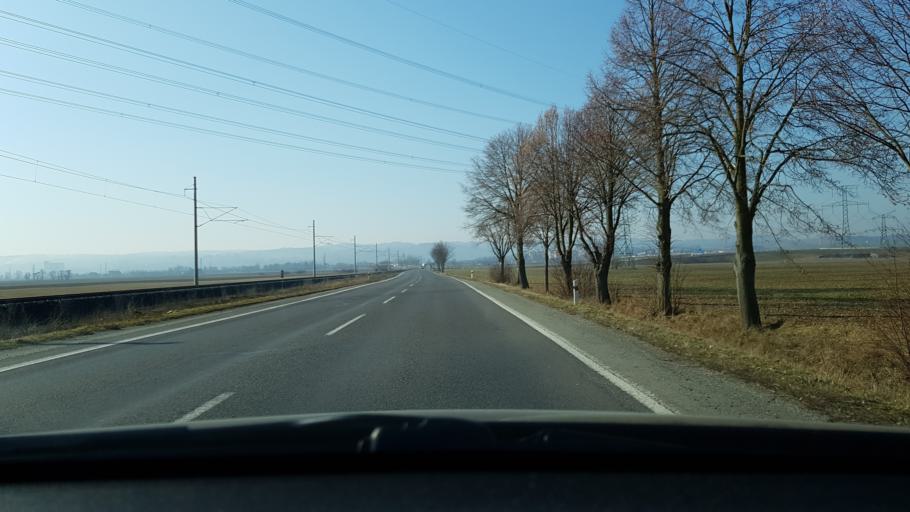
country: CZ
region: Olomoucky
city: Postrelmov
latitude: 49.8965
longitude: 16.9023
